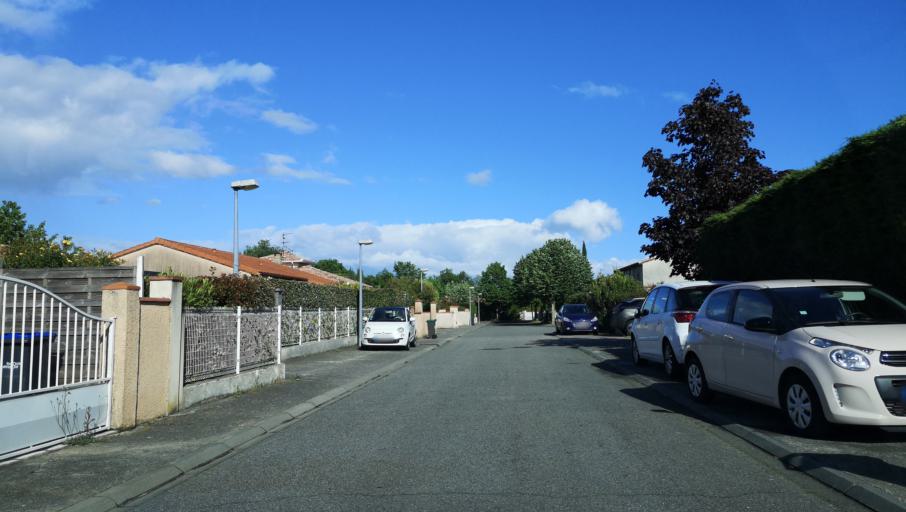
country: FR
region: Midi-Pyrenees
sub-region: Departement de la Haute-Garonne
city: Pibrac
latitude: 43.6228
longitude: 1.3035
